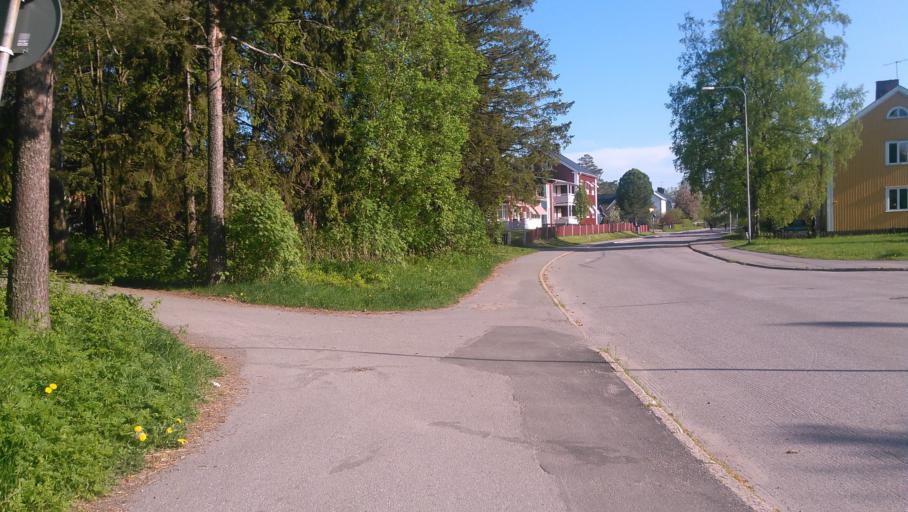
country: SE
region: Vaesterbotten
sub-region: Umea Kommun
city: Umea
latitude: 63.8129
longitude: 20.2991
